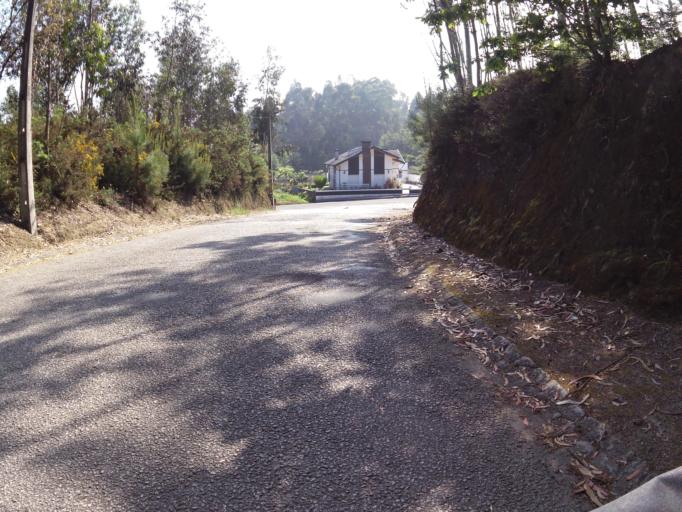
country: PT
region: Aveiro
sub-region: Santa Maria da Feira
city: Argoncilhe
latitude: 41.0358
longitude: -8.5422
